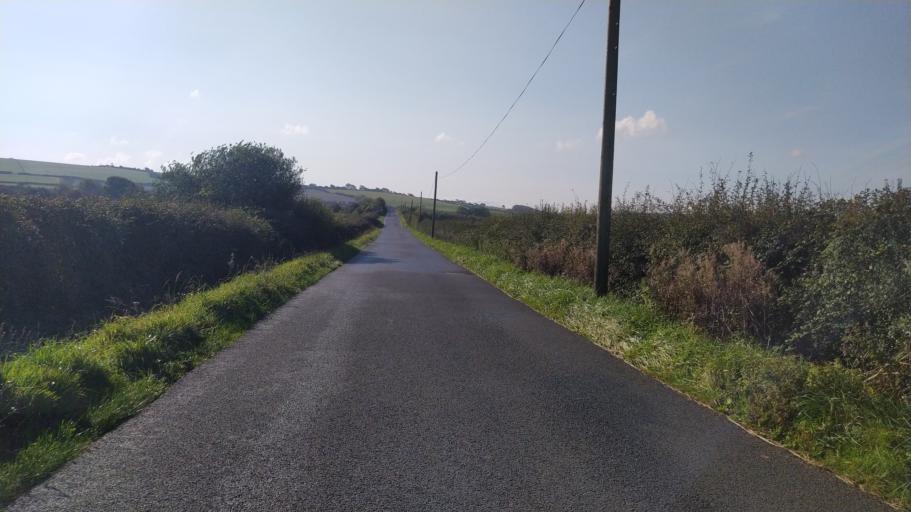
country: GB
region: England
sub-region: Isle of Wight
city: Northwood
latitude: 50.6987
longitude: -1.3463
